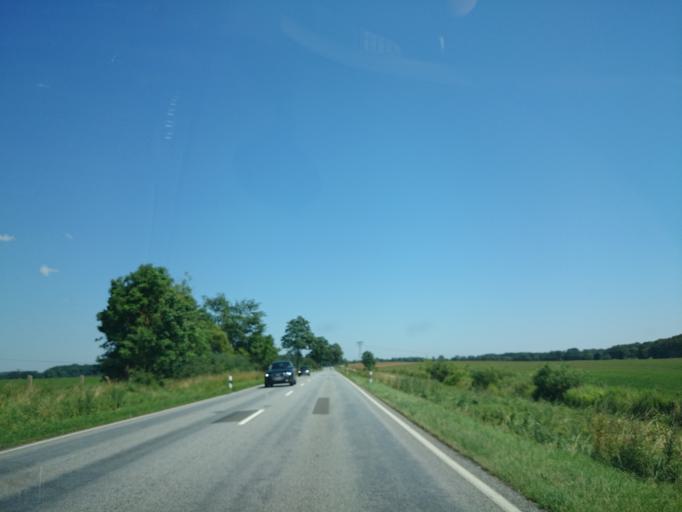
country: DE
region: Mecklenburg-Vorpommern
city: Broderstorf
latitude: 54.0789
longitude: 12.2757
